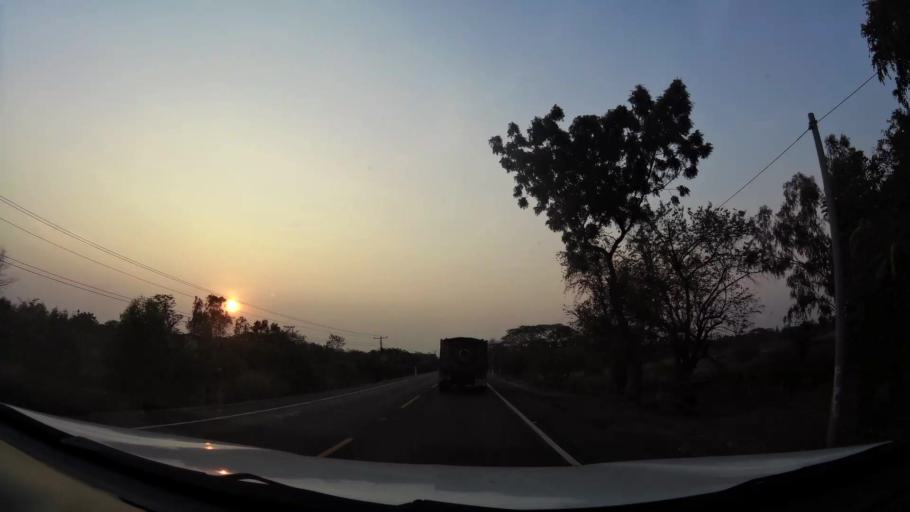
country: NI
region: Leon
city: La Paz Centro
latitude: 12.3108
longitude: -86.7838
